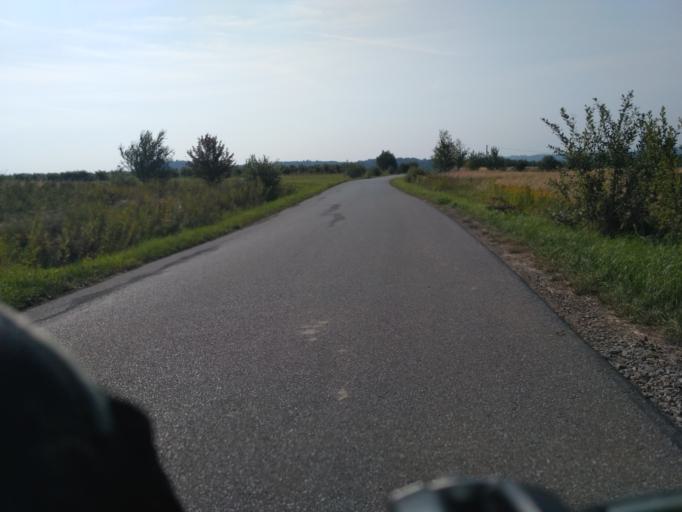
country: PL
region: Subcarpathian Voivodeship
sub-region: Powiat brzozowski
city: Golcowa
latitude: 49.7997
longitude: 22.0256
